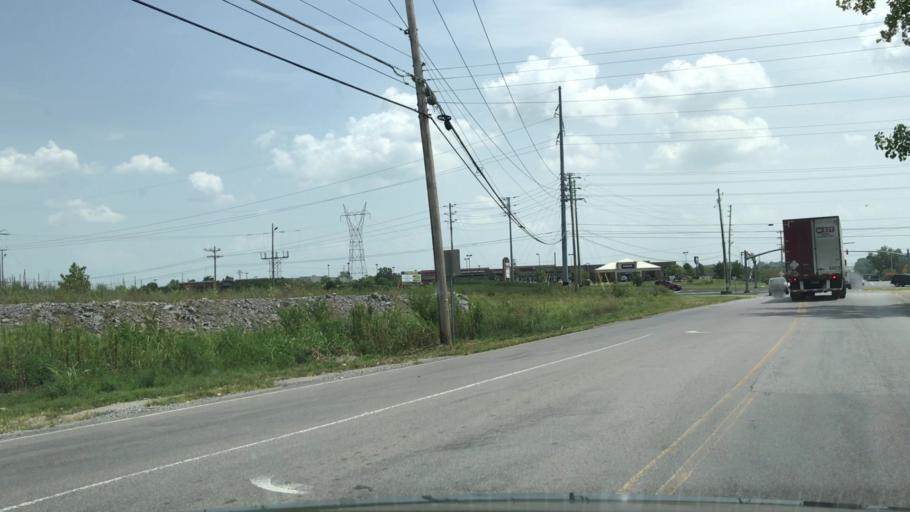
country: US
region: Tennessee
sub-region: Rutherford County
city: Smyrna
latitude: 35.9876
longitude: -86.5499
